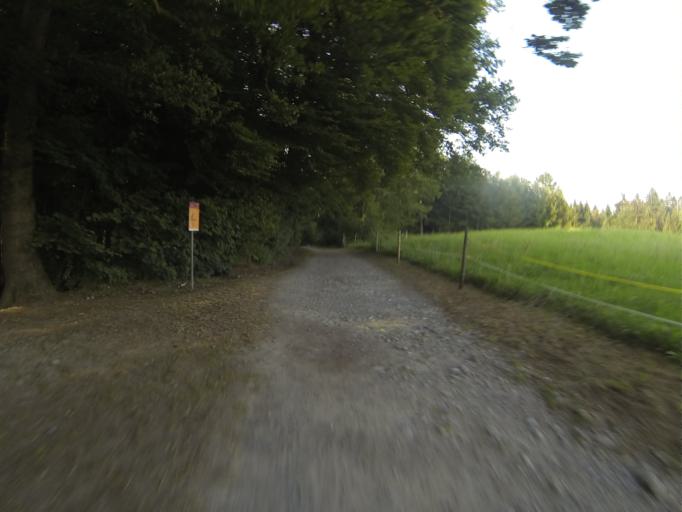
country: CH
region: Lucerne
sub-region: Lucerne-Land District
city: Buchrain
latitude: 47.0897
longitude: 8.3394
